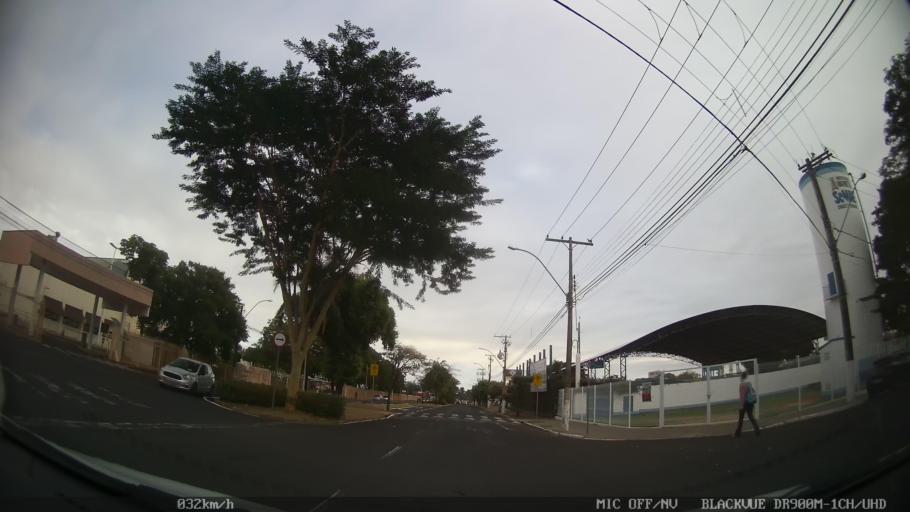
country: BR
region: Sao Paulo
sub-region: Sao Jose Do Rio Preto
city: Sao Jose do Rio Preto
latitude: -20.8334
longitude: -49.3977
